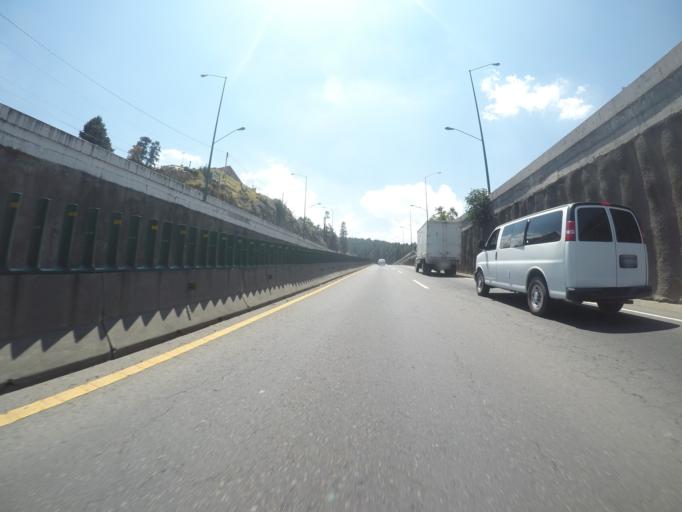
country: MX
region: Mexico City
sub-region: Cuajimalpa de Morelos
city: San Lorenzo Acopilco
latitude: 19.3072
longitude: -99.3359
